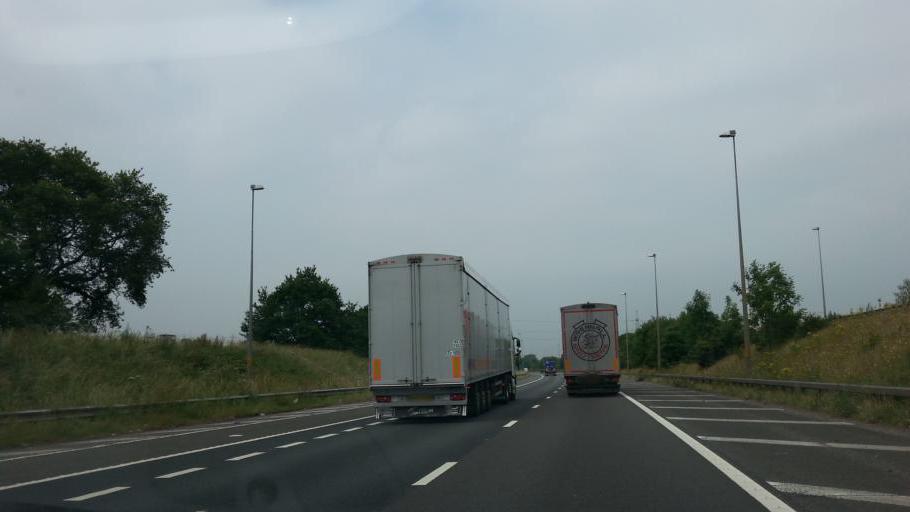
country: GB
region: England
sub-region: Staffordshire
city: Featherstone
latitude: 52.6635
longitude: -2.0675
